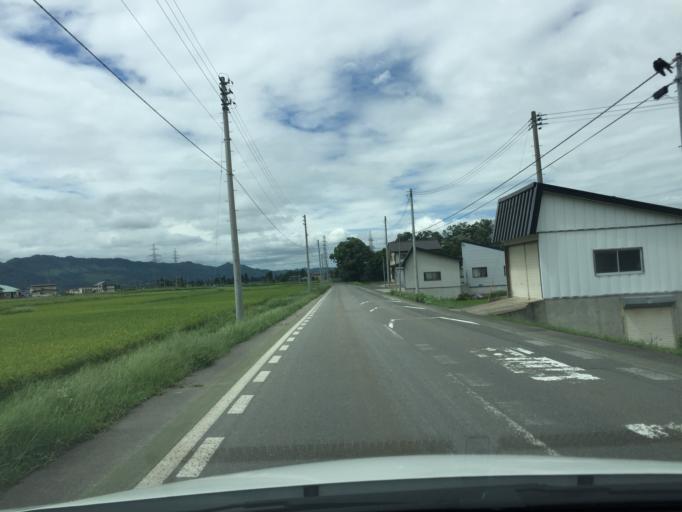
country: JP
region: Yamagata
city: Yonezawa
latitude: 37.8671
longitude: 140.1490
